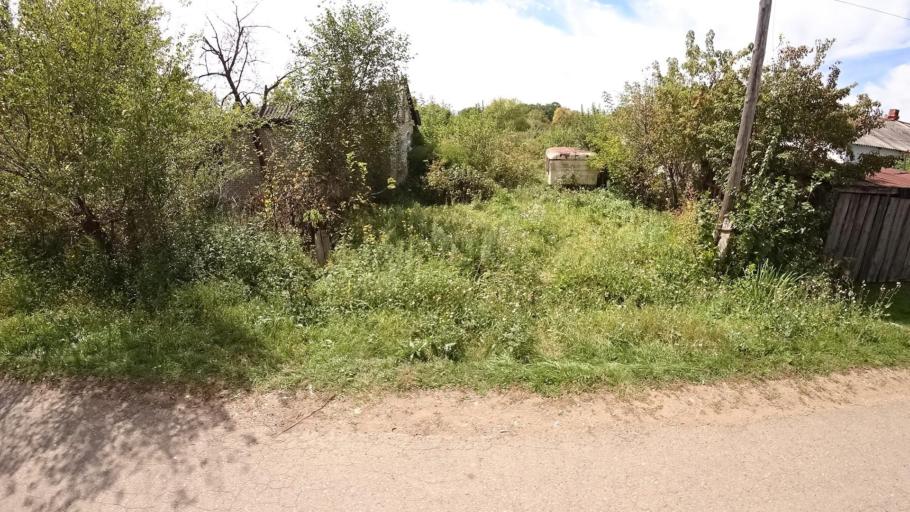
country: RU
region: Primorskiy
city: Yakovlevka
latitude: 44.6450
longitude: 133.5925
